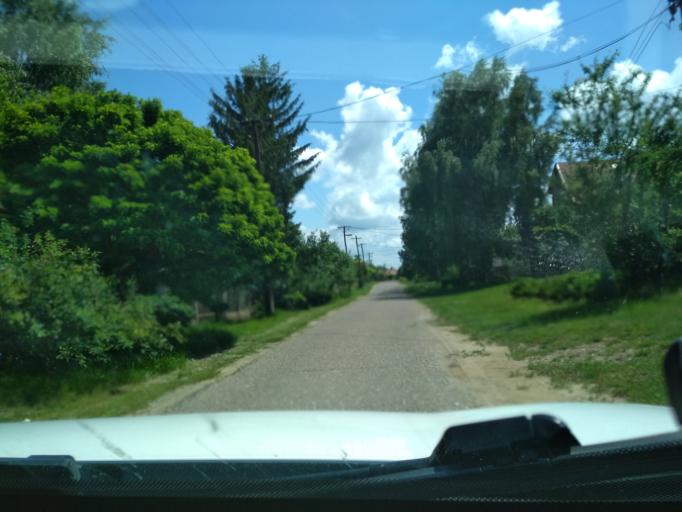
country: HU
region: Jasz-Nagykun-Szolnok
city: Tiszafured
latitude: 47.6056
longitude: 20.7542
